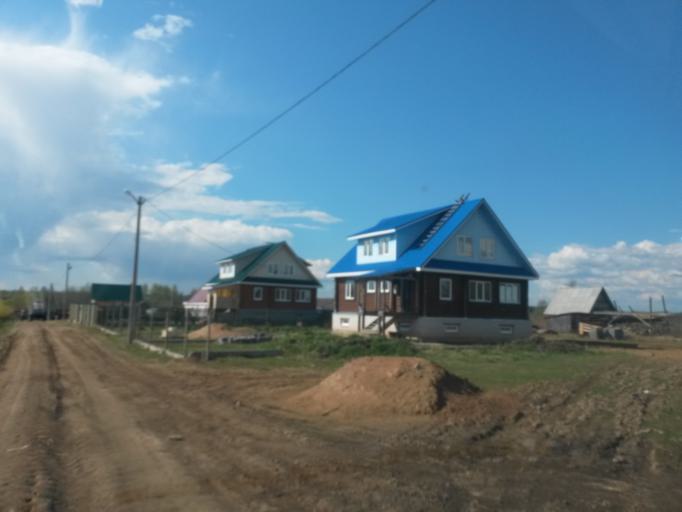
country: RU
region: Jaroslavl
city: Tutayev
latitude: 57.9462
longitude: 39.4387
